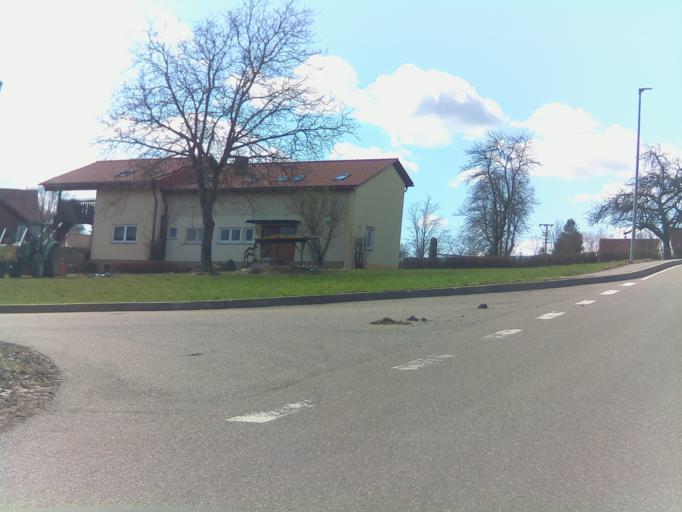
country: DE
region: Baden-Wuerttemberg
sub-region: Regierungsbezirk Stuttgart
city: Mainhardt
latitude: 49.0365
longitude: 9.5593
